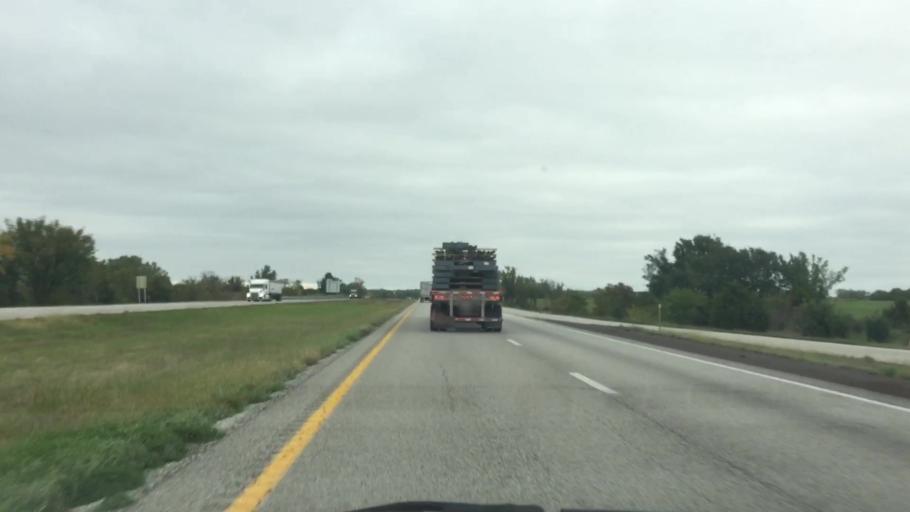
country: US
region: Missouri
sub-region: Clinton County
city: Cameron
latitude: 39.8558
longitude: -94.1757
